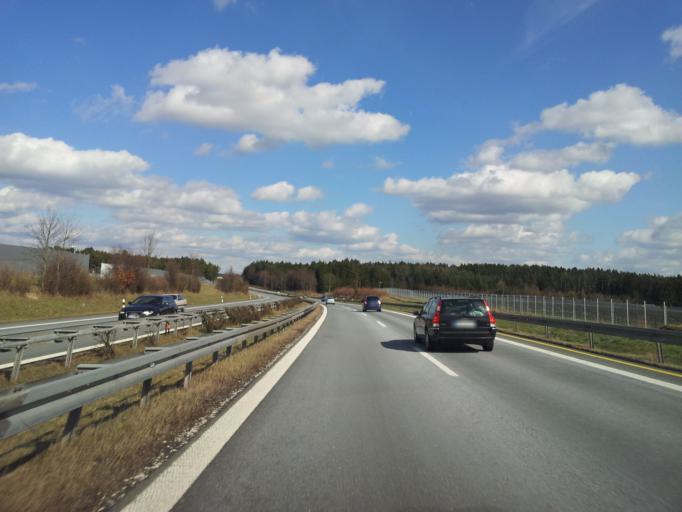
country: DE
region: Bavaria
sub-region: Upper Franconia
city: Wonsees
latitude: 50.0054
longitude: 11.2625
